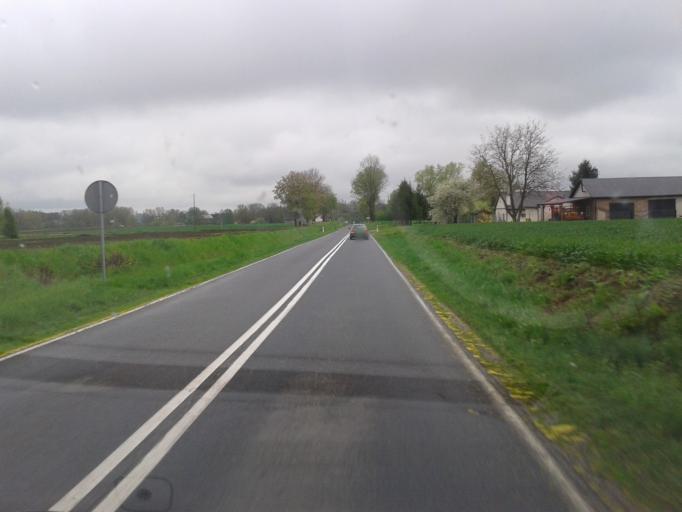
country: PL
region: Lublin Voivodeship
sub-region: Powiat hrubieszowski
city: Mircze
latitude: 50.5633
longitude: 23.9376
